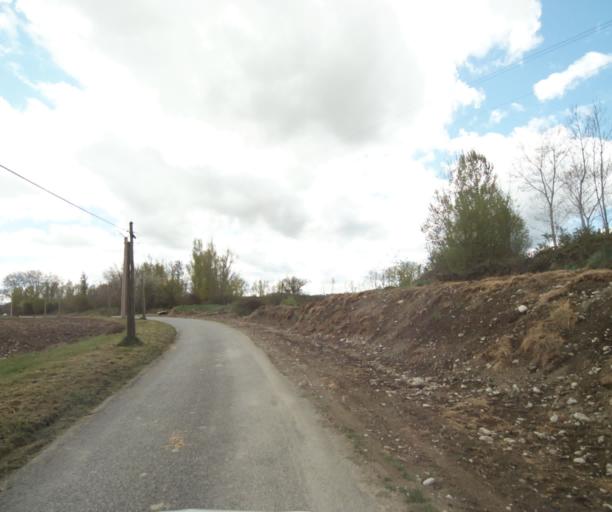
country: FR
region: Midi-Pyrenees
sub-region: Departement de l'Ariege
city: Saverdun
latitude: 43.2531
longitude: 1.5819
